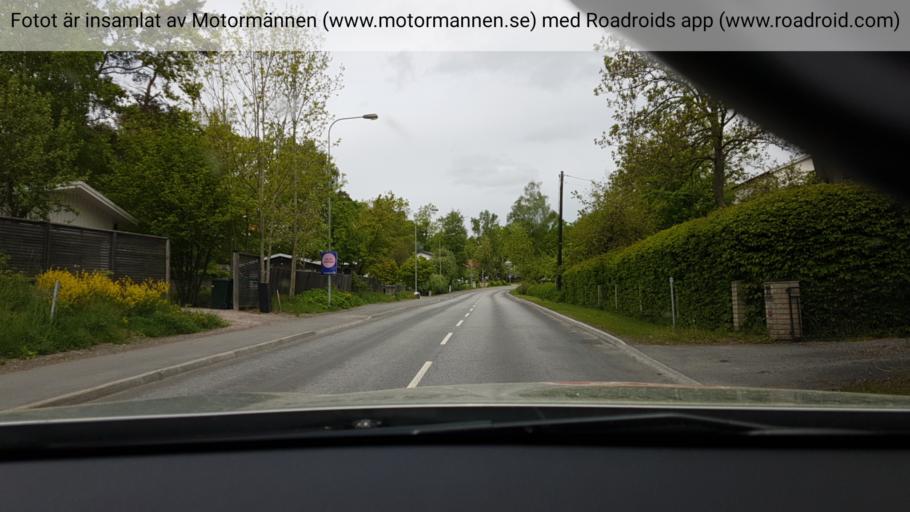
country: SE
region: Stockholm
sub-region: Nacka Kommun
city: Saltsjobaden
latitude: 59.2662
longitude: 18.3067
